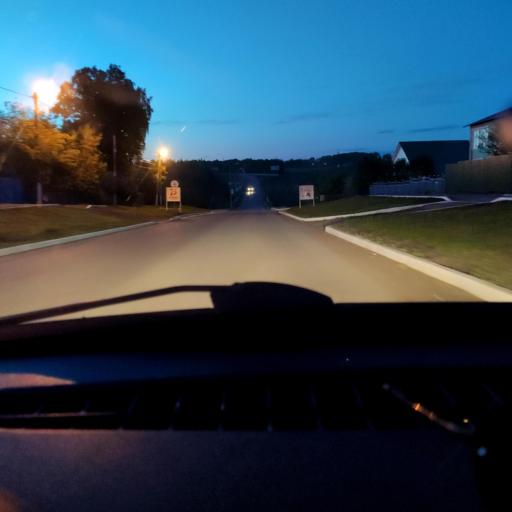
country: RU
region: Bashkortostan
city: Karmaskaly
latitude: 54.3725
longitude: 56.1727
